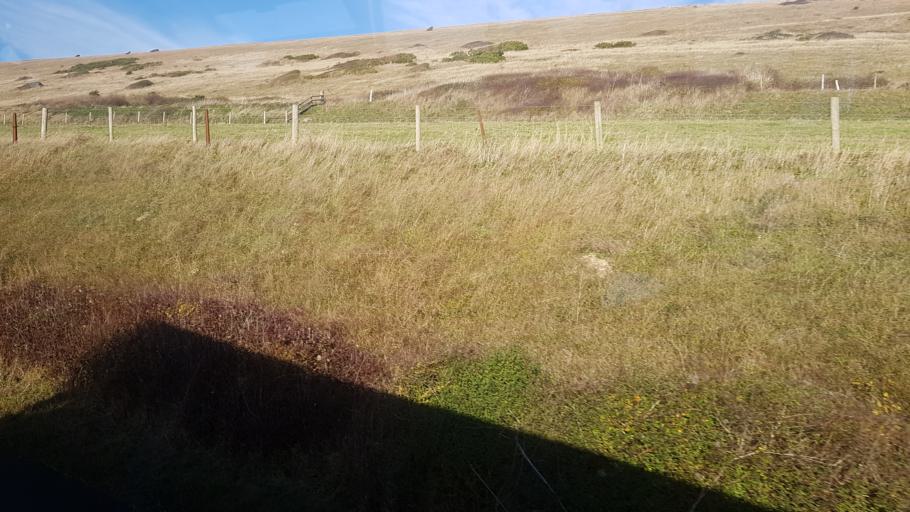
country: GB
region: England
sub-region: Isle of Wight
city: Freshwater
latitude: 50.6668
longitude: -1.4788
